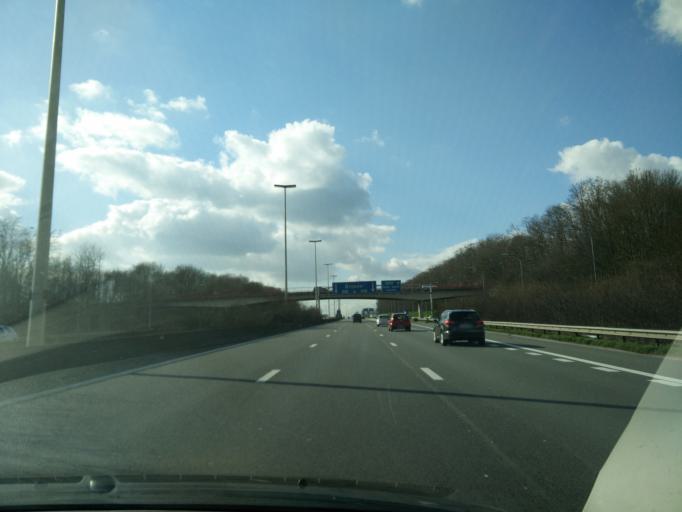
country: BE
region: Flanders
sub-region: Provincie Vlaams-Brabant
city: Oud-Heverlee
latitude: 50.8542
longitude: 4.6548
